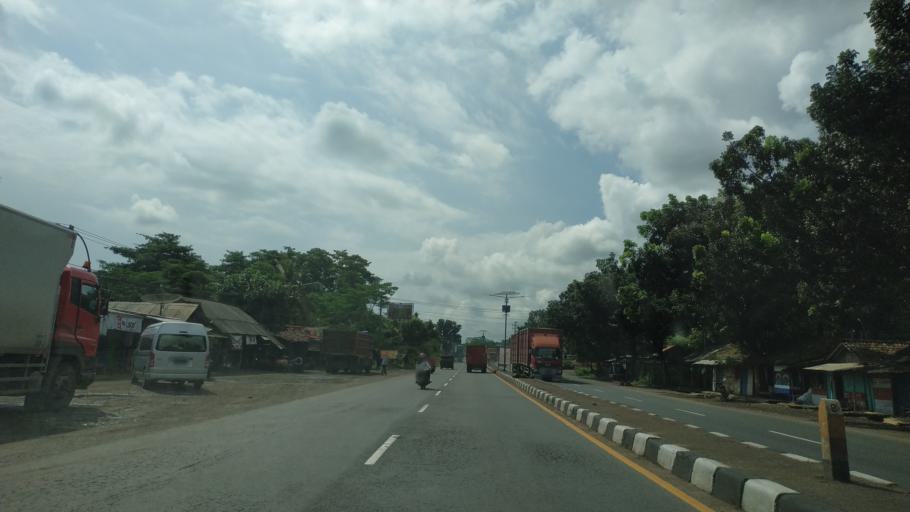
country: ID
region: Central Java
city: Pekalongan
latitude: -6.9326
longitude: 109.7672
